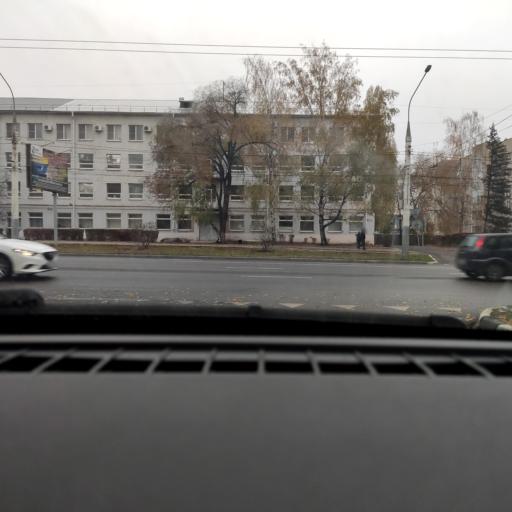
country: RU
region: Voronezj
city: Voronezh
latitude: 51.6575
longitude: 39.2453
